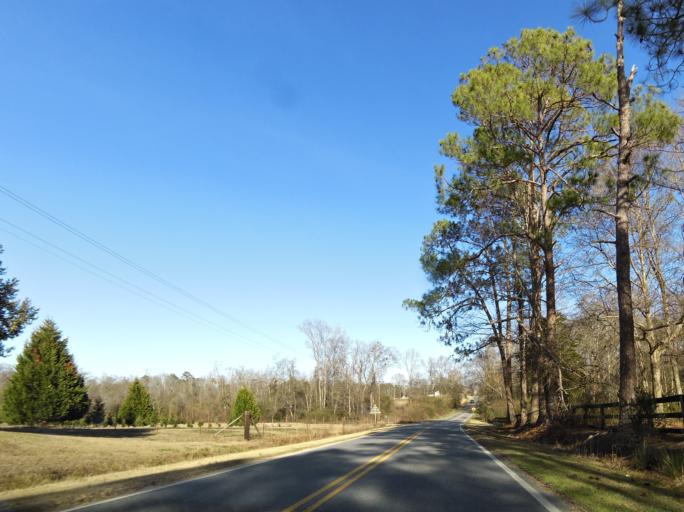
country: US
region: Georgia
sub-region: Bibb County
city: West Point
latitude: 32.7755
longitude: -83.8247
